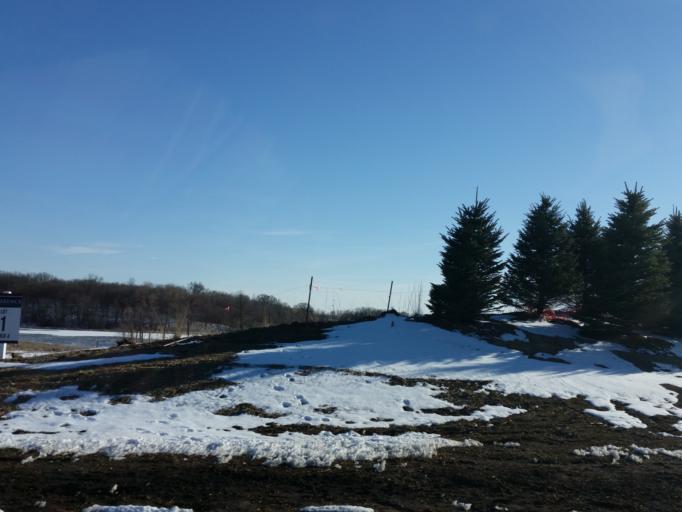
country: US
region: Minnesota
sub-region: Scott County
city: Elko New Market
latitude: 44.6291
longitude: -93.3665
